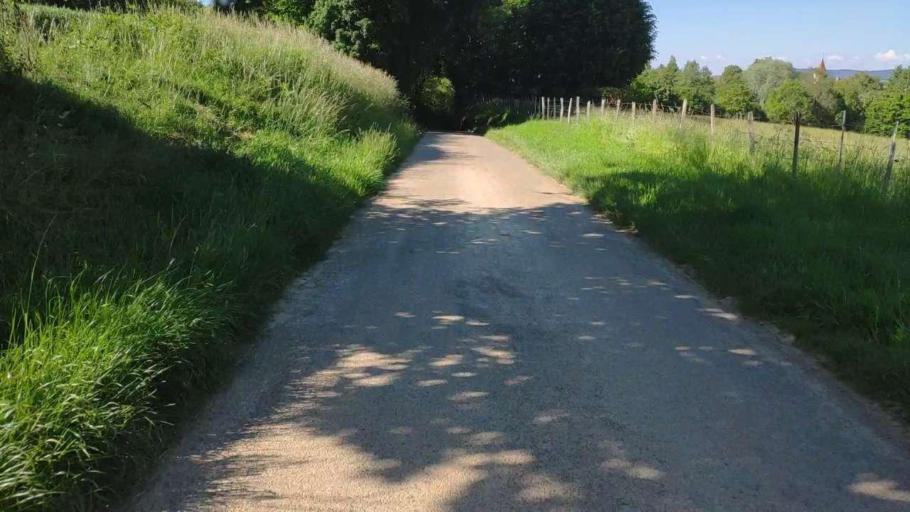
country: FR
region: Franche-Comte
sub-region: Departement du Jura
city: Montmorot
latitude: 46.7268
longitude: 5.5519
